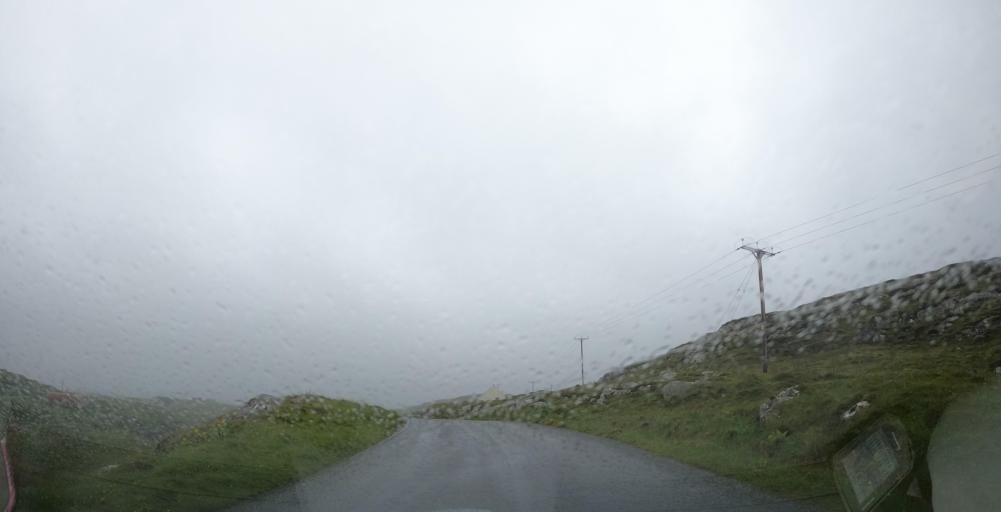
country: GB
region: Scotland
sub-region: Eilean Siar
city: Barra
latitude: 57.0128
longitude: -7.4303
